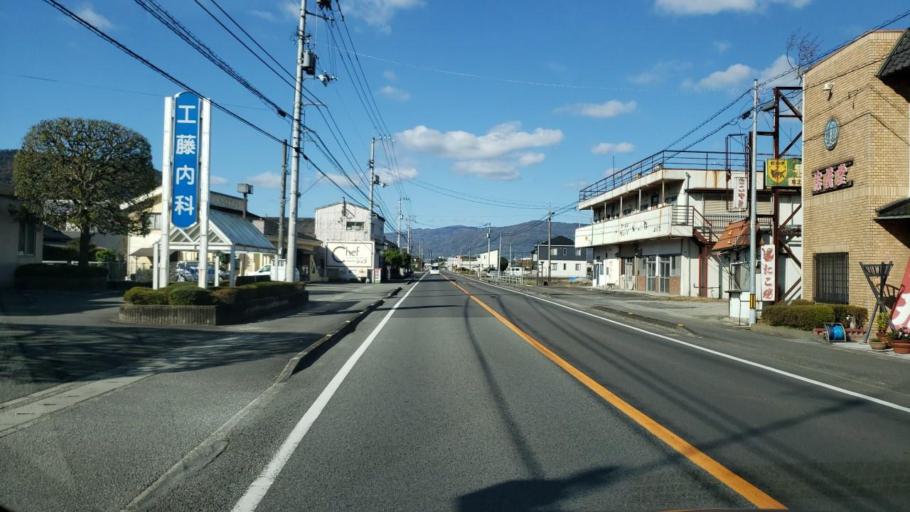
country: JP
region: Tokushima
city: Wakimachi
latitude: 34.0585
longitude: 134.2207
